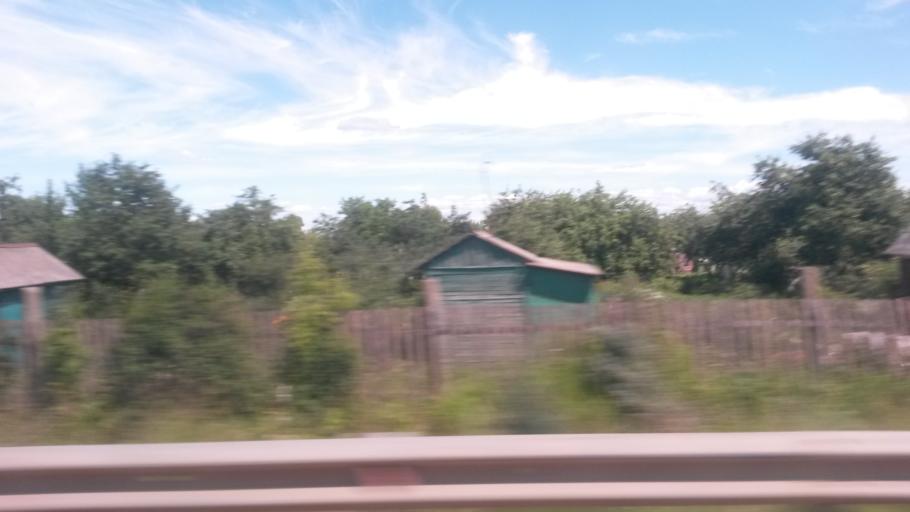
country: RU
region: Ivanovo
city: Staraya Vichuga
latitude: 57.2191
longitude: 41.8631
